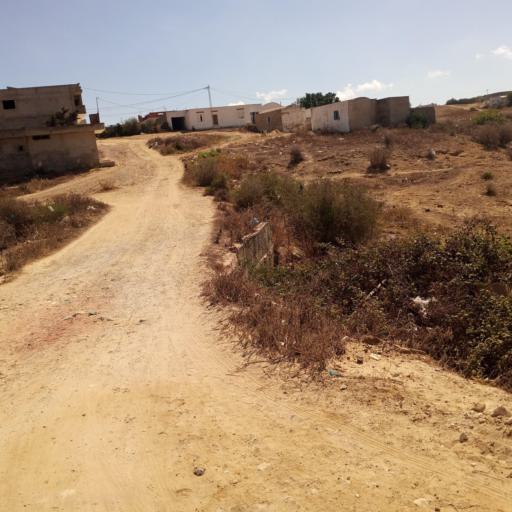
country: TN
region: Nabul
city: Qulaybiyah
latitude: 36.8577
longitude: 11.0332
